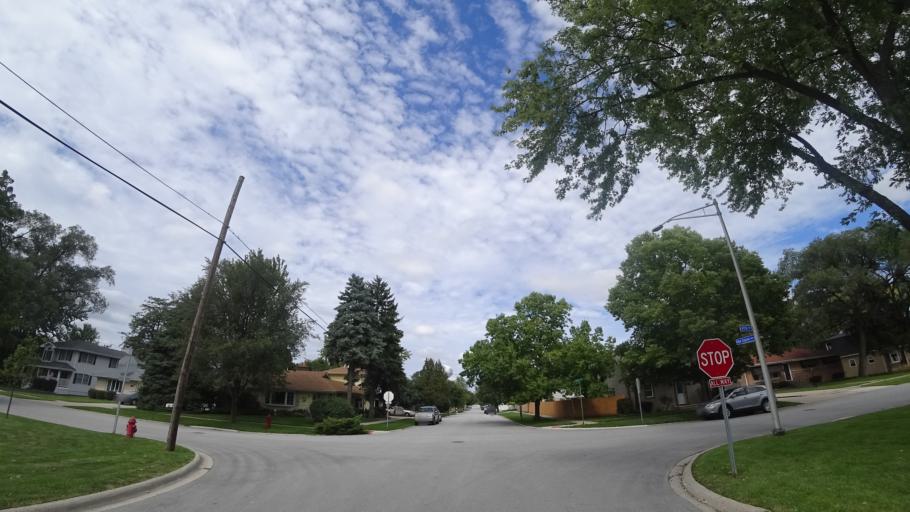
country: US
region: Illinois
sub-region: Cook County
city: Chicago Ridge
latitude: 41.7155
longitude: -87.7917
